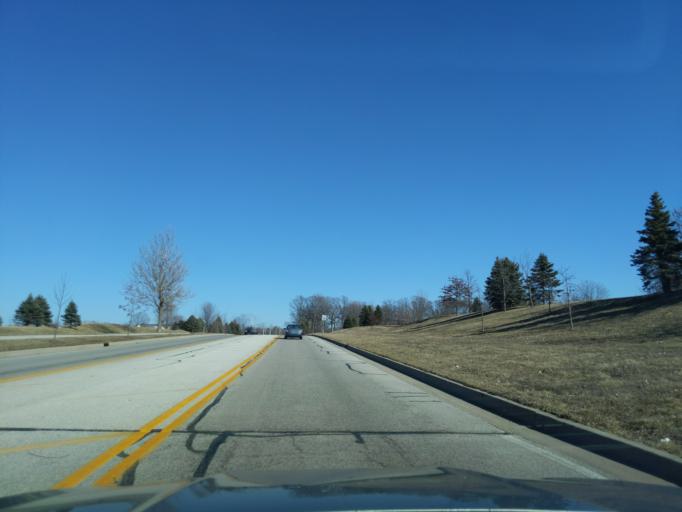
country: US
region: Indiana
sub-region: Tippecanoe County
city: West Lafayette
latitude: 40.4463
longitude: -86.9278
